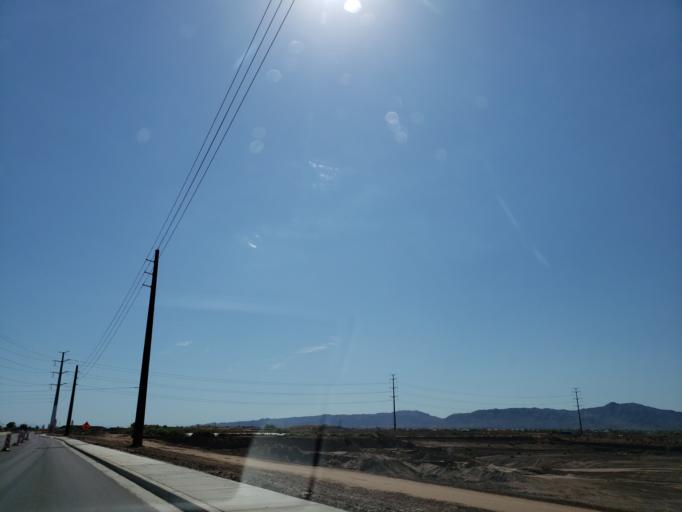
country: US
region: Arizona
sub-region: Maricopa County
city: Laveen
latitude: 33.4079
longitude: -112.1893
